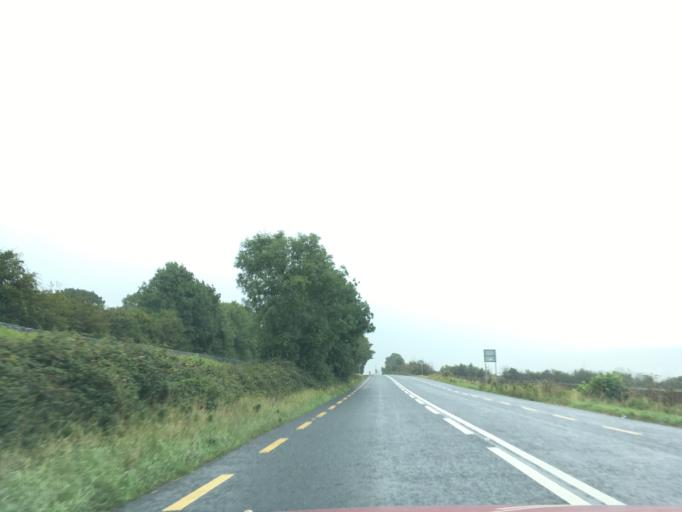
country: IE
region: Munster
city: Carrick-on-Suir
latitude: 52.3524
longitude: -7.4692
